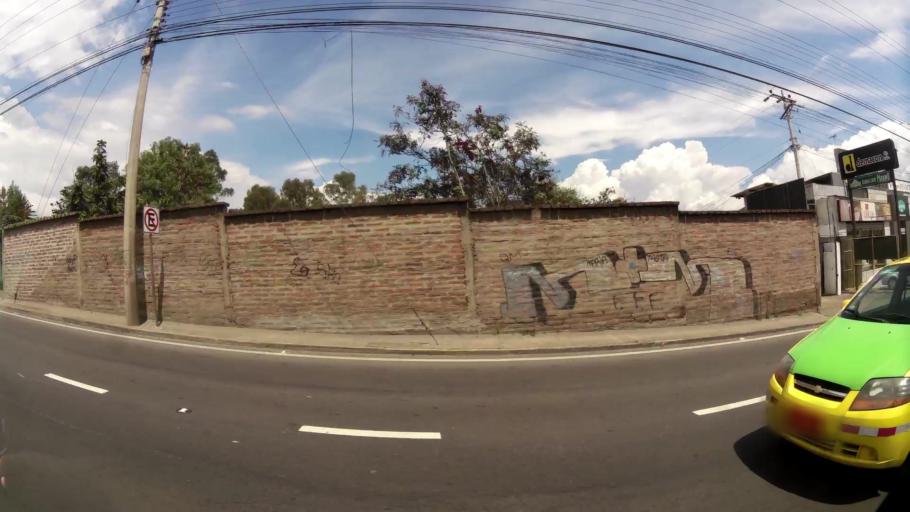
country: EC
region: Pichincha
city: Sangolqui
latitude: -0.2124
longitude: -78.3621
